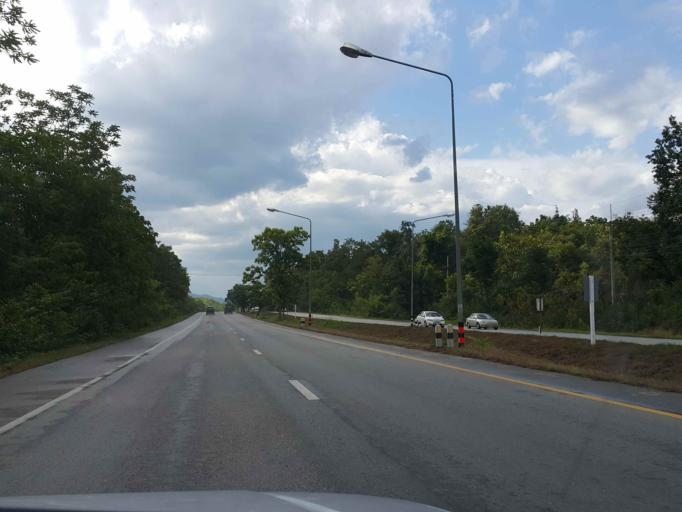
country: TH
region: Lampang
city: Thoen
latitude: 17.6778
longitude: 99.2421
